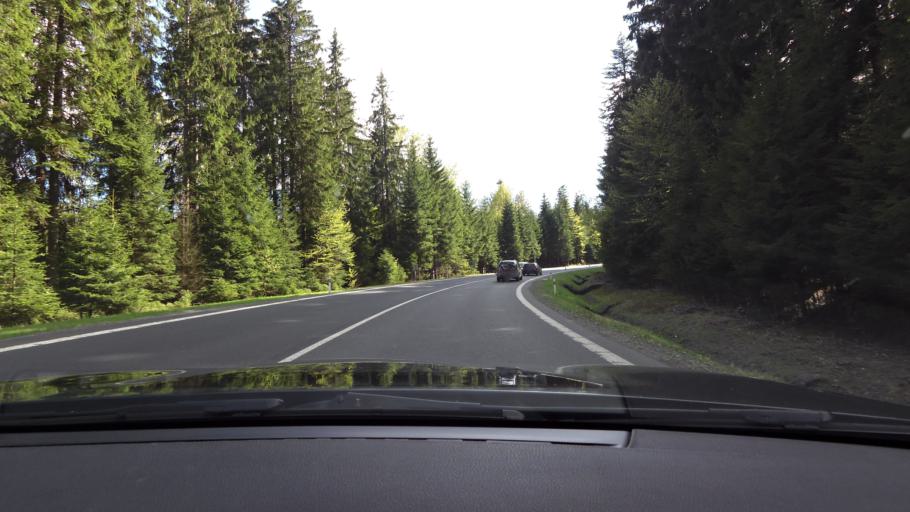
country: CZ
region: Plzensky
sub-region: Okres Klatovy
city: Zelezna Ruda
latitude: 49.1859
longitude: 13.3066
